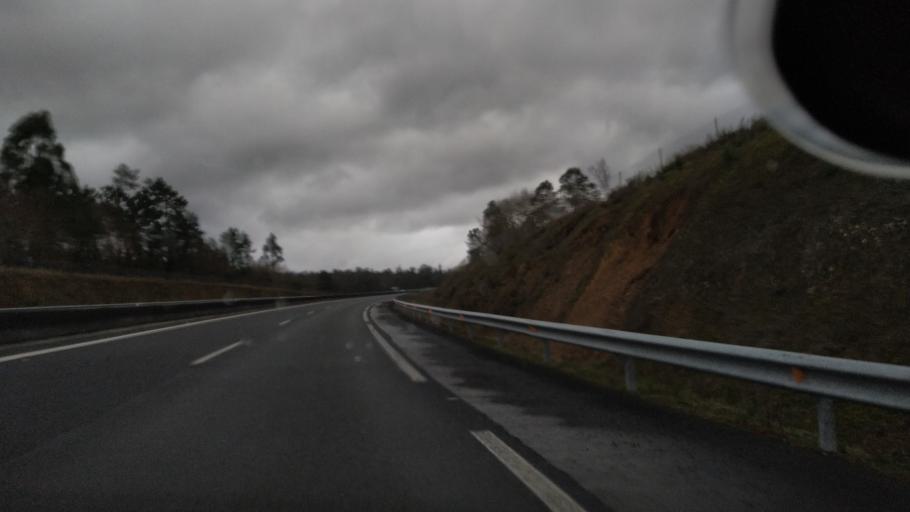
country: ES
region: Galicia
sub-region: Provincia da Coruna
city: Vedra
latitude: 42.8148
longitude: -8.4855
